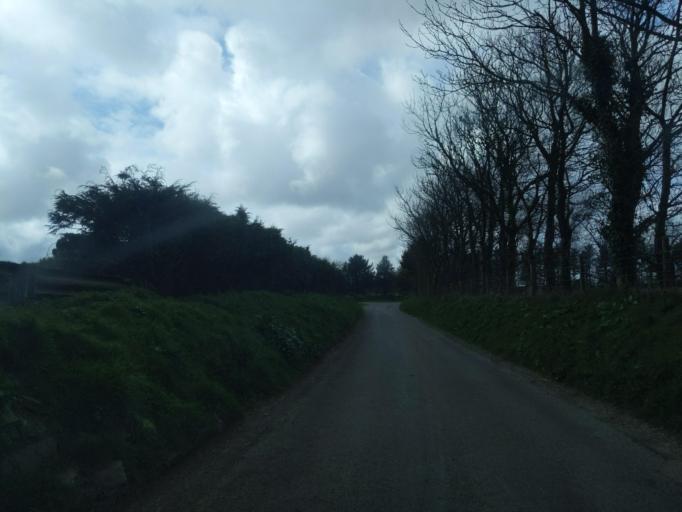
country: GB
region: England
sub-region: Cornwall
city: Camelford
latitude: 50.6243
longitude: -4.5744
